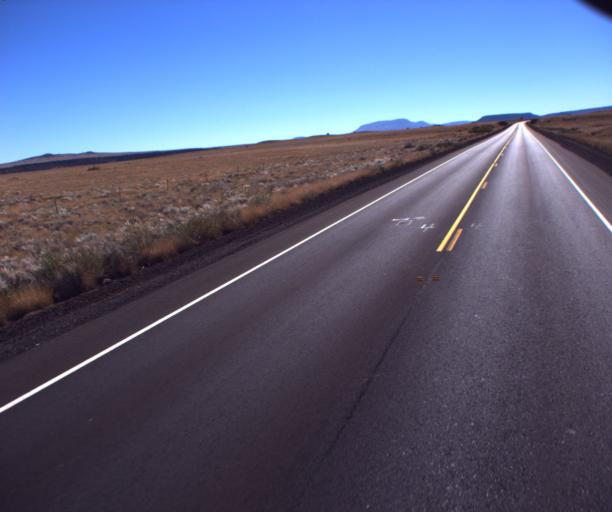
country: US
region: Arizona
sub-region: Apache County
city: Springerville
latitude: 34.2052
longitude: -109.3276
